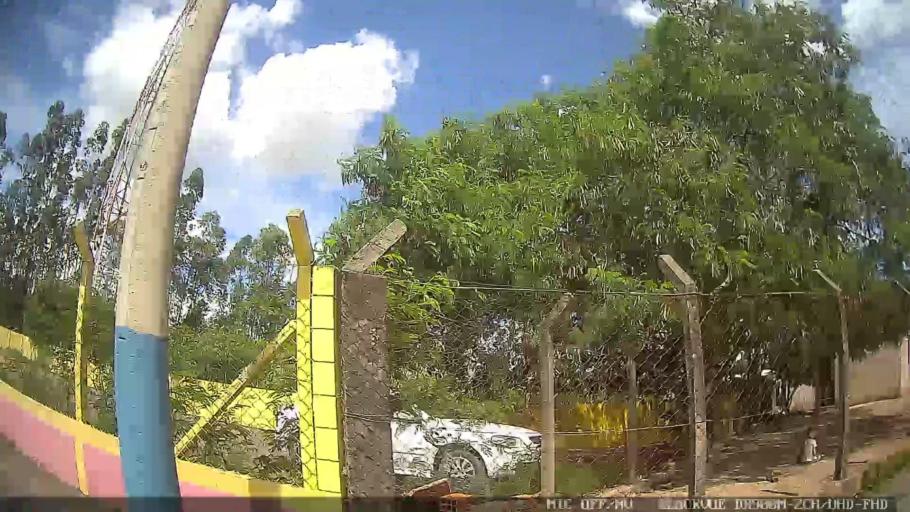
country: BR
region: Sao Paulo
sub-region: Conchas
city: Conchas
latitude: -23.0291
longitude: -48.0160
